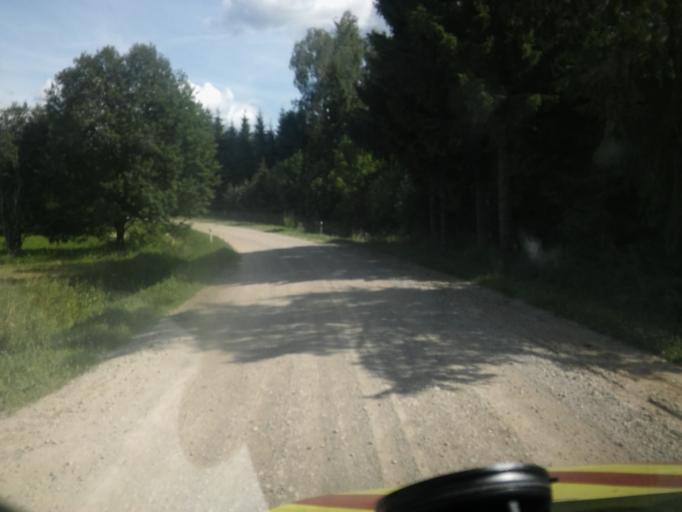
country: EE
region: Viljandimaa
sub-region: Karksi vald
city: Karksi-Nuia
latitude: 58.0584
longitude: 25.5427
